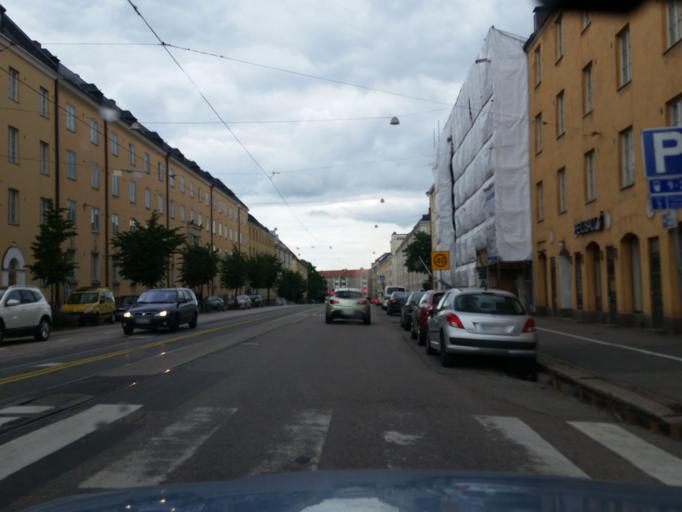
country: FI
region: Uusimaa
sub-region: Helsinki
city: Helsinki
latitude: 60.1946
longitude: 24.9573
